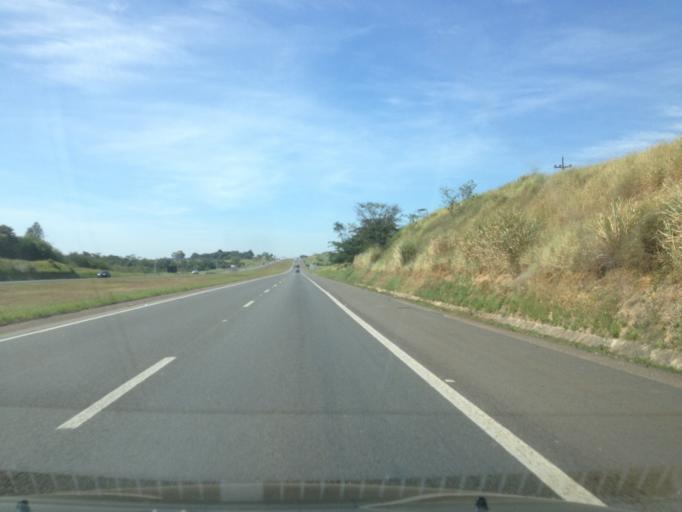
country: BR
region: Sao Paulo
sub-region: Tatui
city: Tatui
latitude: -23.2551
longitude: -47.9215
